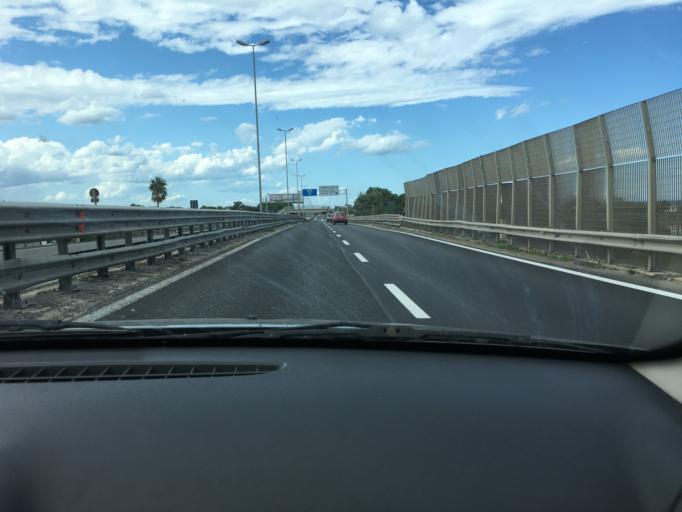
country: IT
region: Apulia
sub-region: Provincia di Bari
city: San Paolo
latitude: 41.1382
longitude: 16.8063
